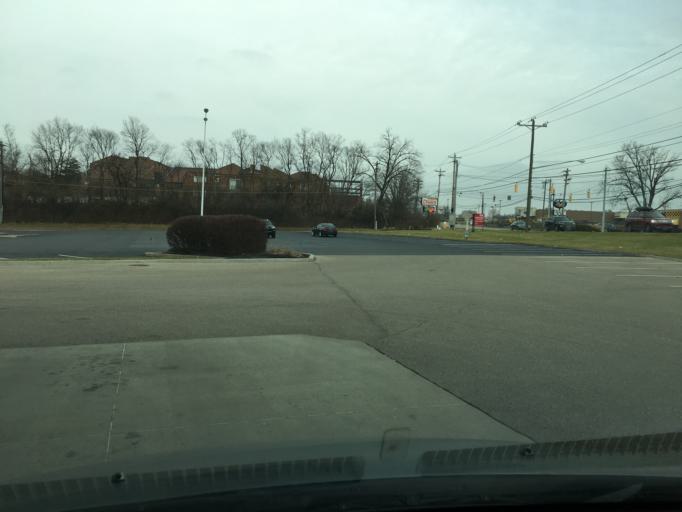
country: US
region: Ohio
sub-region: Hamilton County
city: Sharonville
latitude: 39.2931
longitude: -84.3939
